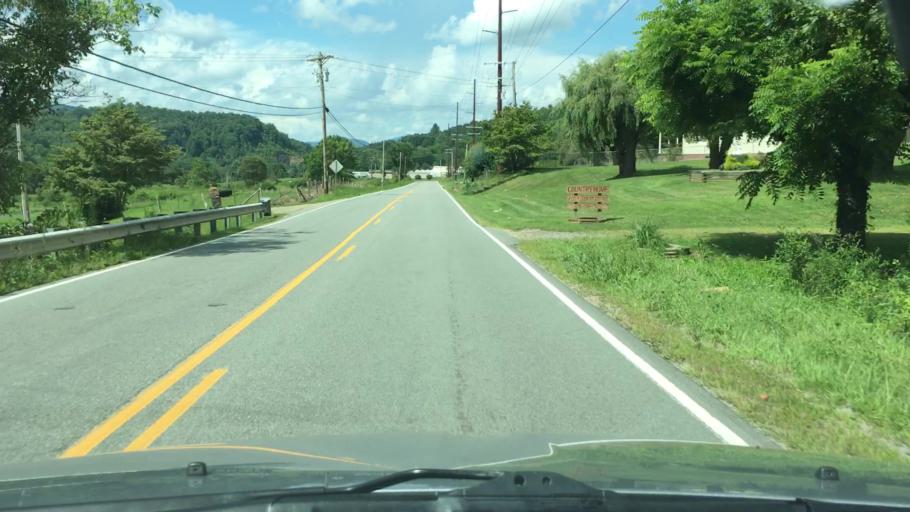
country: US
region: North Carolina
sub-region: Yancey County
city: Burnsville
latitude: 35.8859
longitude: -82.2153
